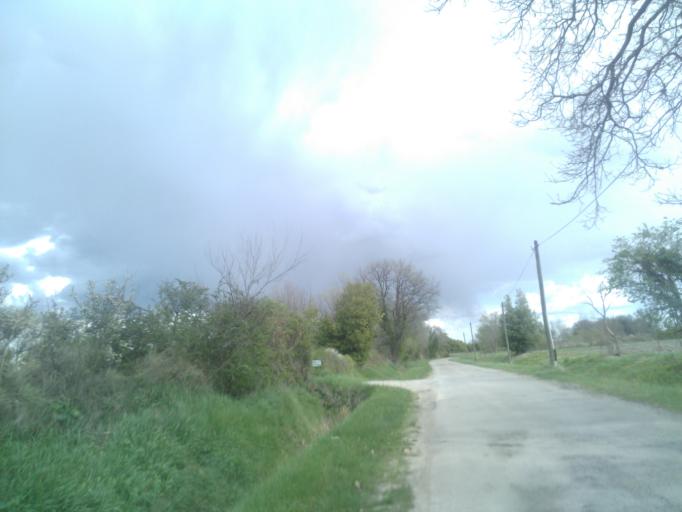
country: FR
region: Provence-Alpes-Cote d'Azur
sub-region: Departement des Bouches-du-Rhone
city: Arles
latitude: 43.6289
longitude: 4.5830
